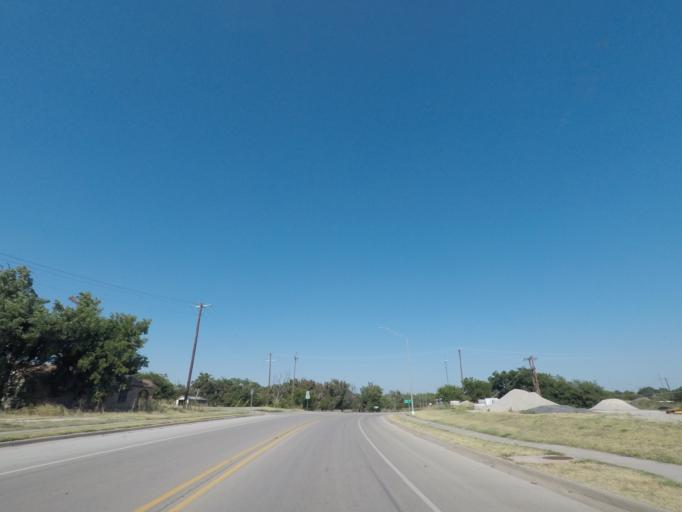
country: US
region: Texas
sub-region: Baylor County
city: Seymour
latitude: 33.5959
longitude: -99.2562
